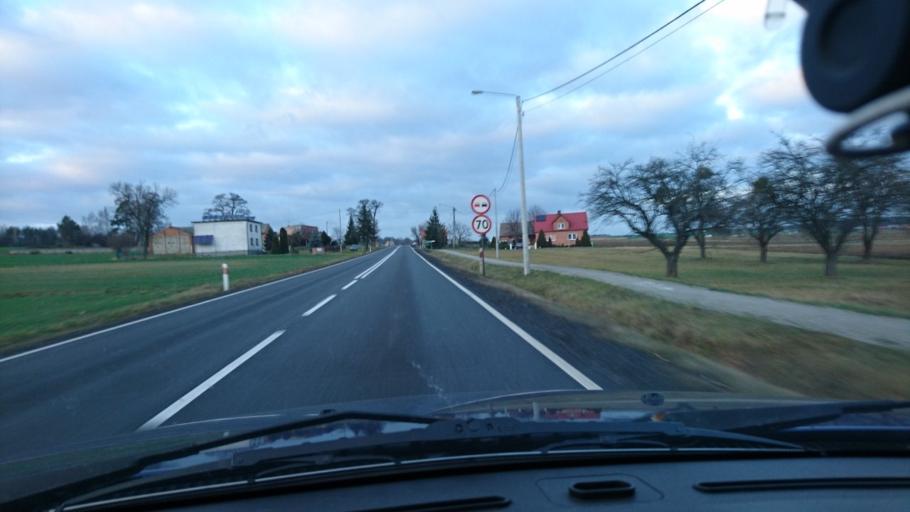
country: PL
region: Greater Poland Voivodeship
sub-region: Powiat ostrzeszowski
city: Ostrzeszow
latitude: 51.3575
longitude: 17.9468
